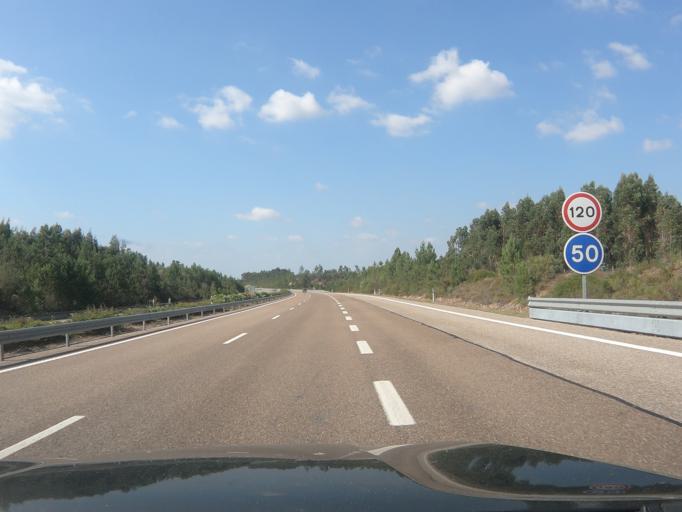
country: PT
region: Santarem
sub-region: Salvaterra de Magos
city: Marinhais
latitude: 39.0564
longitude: -8.6674
